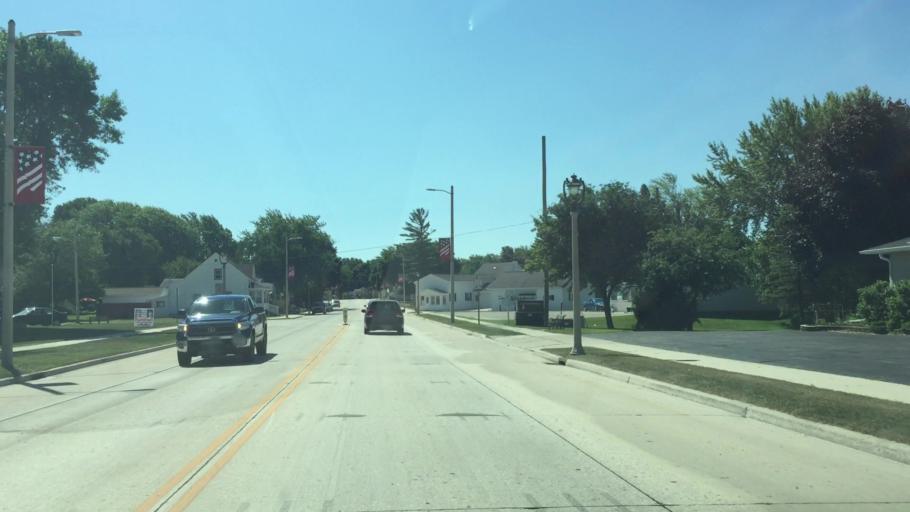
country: US
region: Wisconsin
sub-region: Calumet County
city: New Holstein
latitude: 43.9524
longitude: -88.1021
